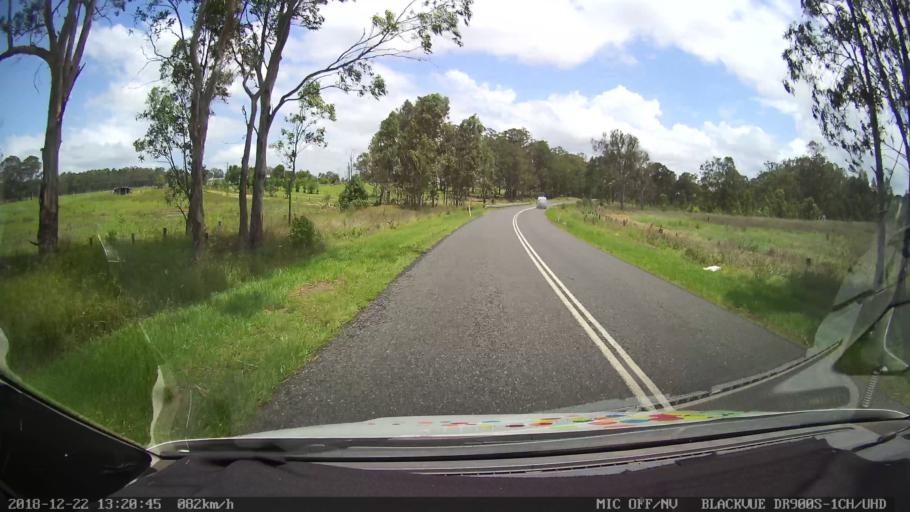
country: AU
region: New South Wales
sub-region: Clarence Valley
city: South Grafton
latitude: -29.7698
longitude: 152.9263
